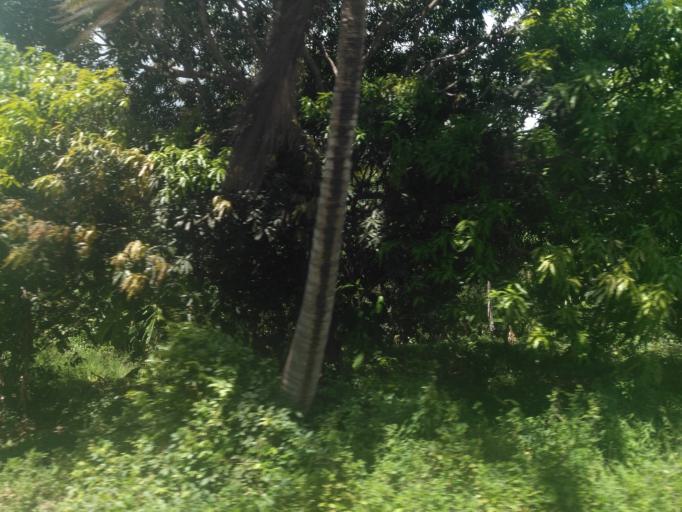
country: TZ
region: Zanzibar North
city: Gamba
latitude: -5.9355
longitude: 39.3413
